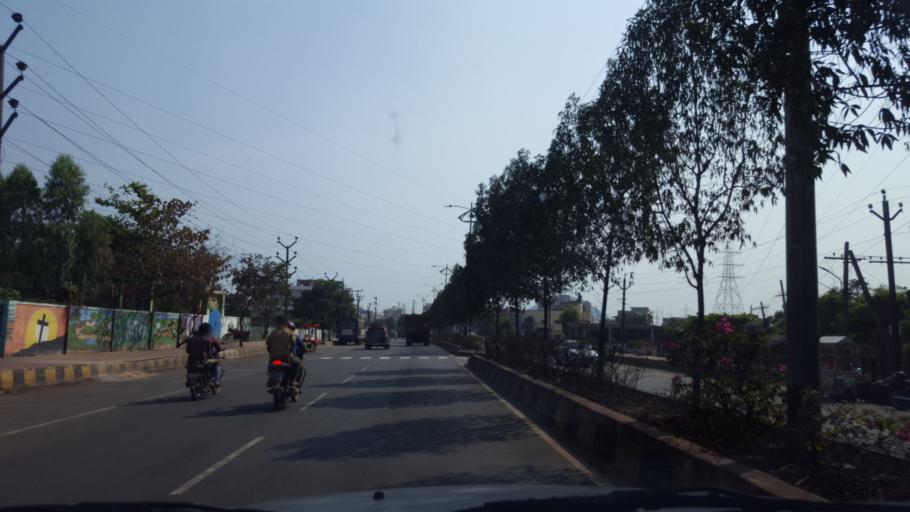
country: IN
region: Andhra Pradesh
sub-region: Vishakhapatnam
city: Visakhapatnam
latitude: 17.6813
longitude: 83.1938
